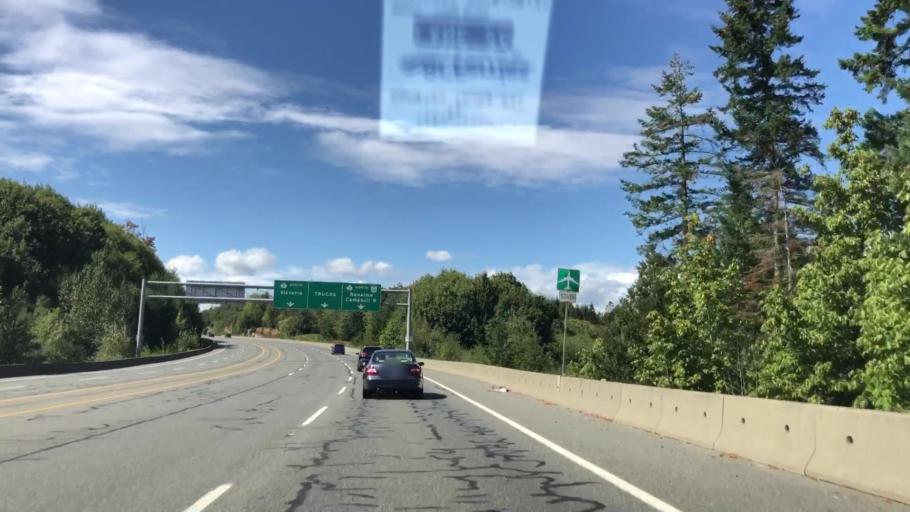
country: CA
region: British Columbia
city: Nanaimo
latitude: 49.1138
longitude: -123.8886
